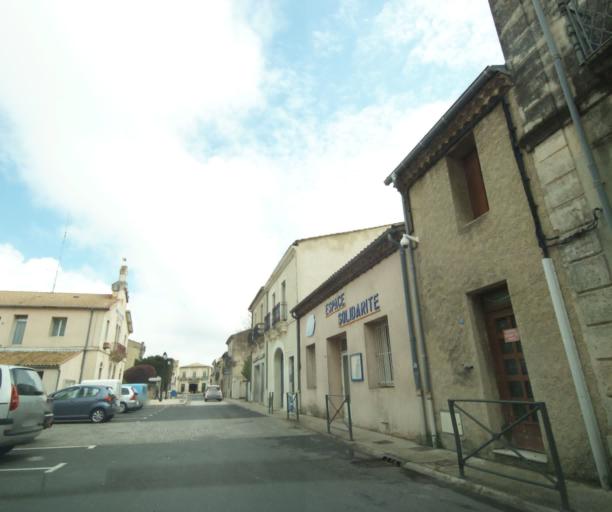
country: FR
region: Languedoc-Roussillon
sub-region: Departement de l'Herault
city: Fabregues
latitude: 43.5497
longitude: 3.7786
